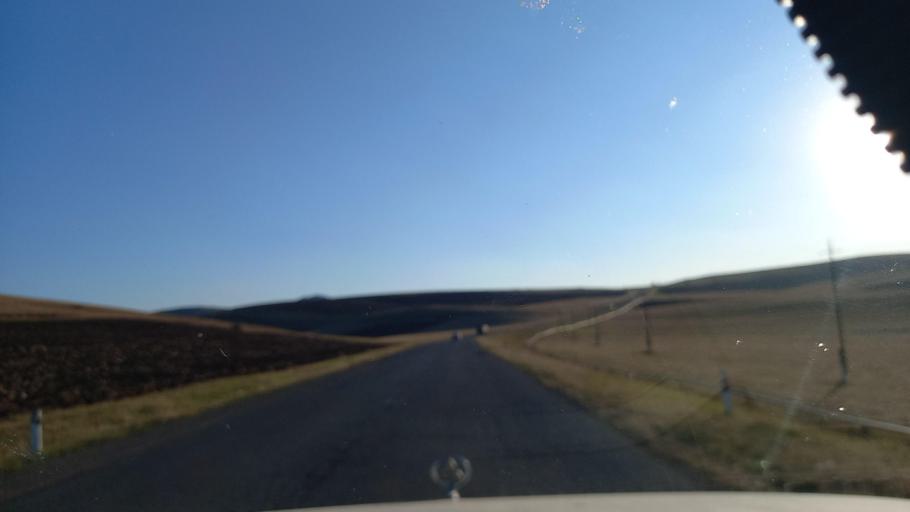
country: AZ
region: Shamkir Rayon
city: Shamkhor
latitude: 40.7622
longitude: 45.9192
